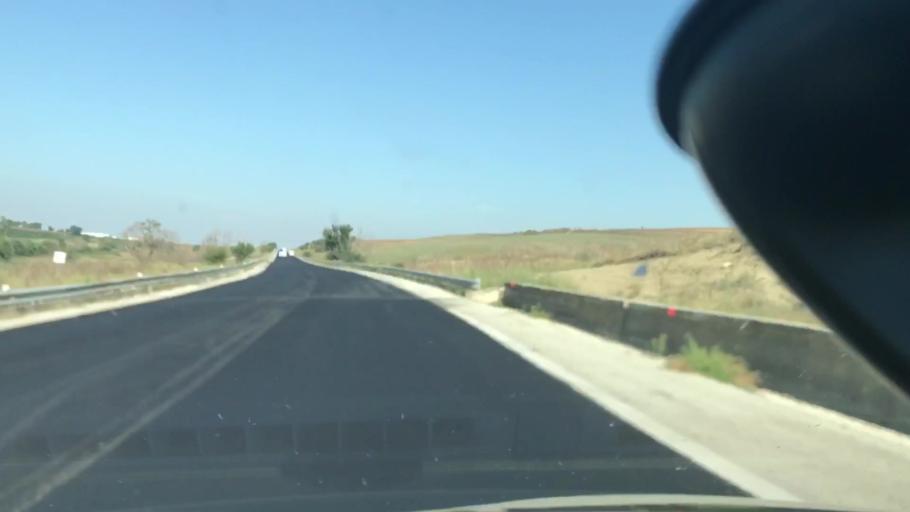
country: IT
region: Apulia
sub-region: Provincia di Barletta - Andria - Trani
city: Spinazzola
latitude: 40.9019
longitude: 16.1193
